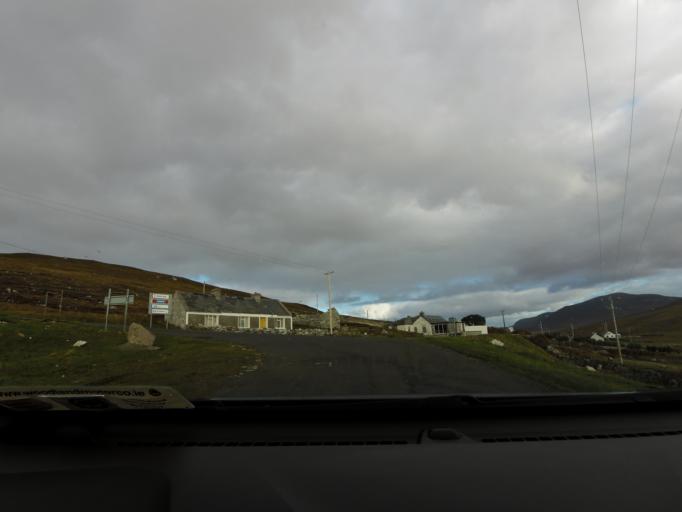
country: IE
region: Connaught
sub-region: Maigh Eo
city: Belmullet
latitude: 53.9064
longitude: -9.9939
